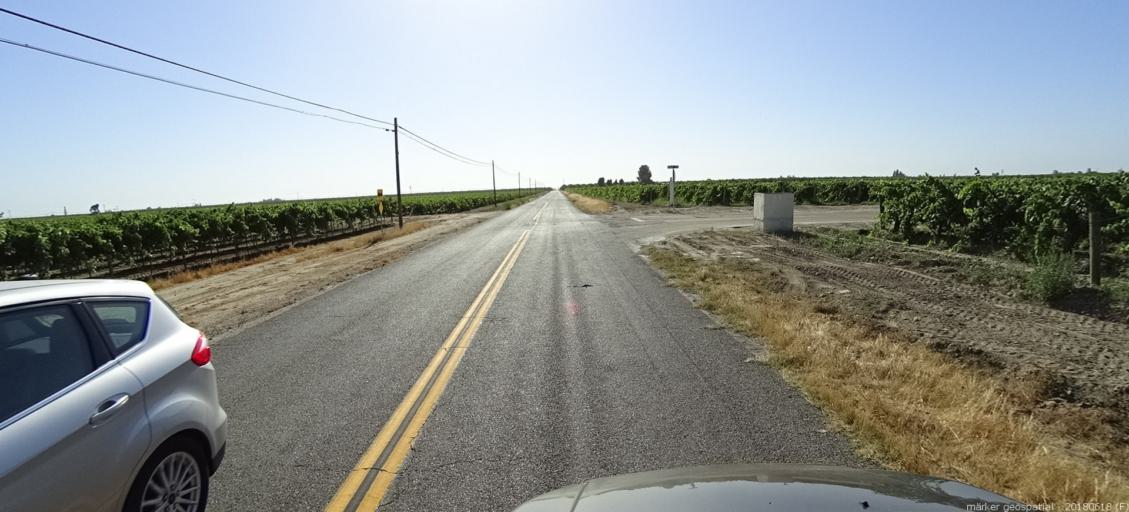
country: US
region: California
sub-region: Fresno County
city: Biola
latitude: 36.8368
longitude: -120.0974
